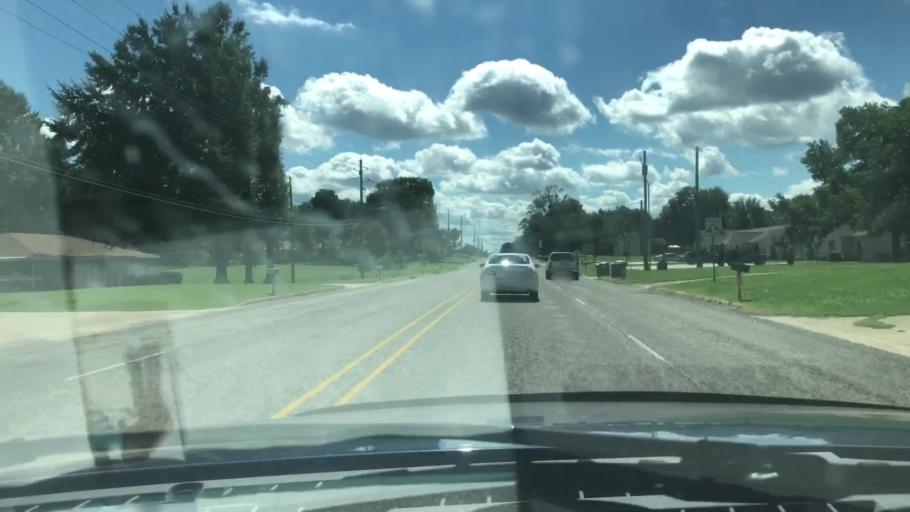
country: US
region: Texas
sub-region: Bowie County
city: Wake Village
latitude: 33.3954
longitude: -94.0921
